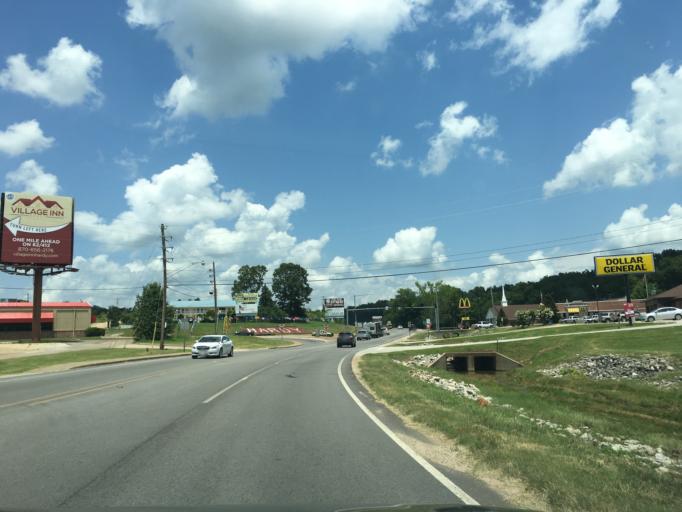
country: US
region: Arkansas
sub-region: Sharp County
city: Cherokee Village
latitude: 36.3163
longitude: -91.4868
